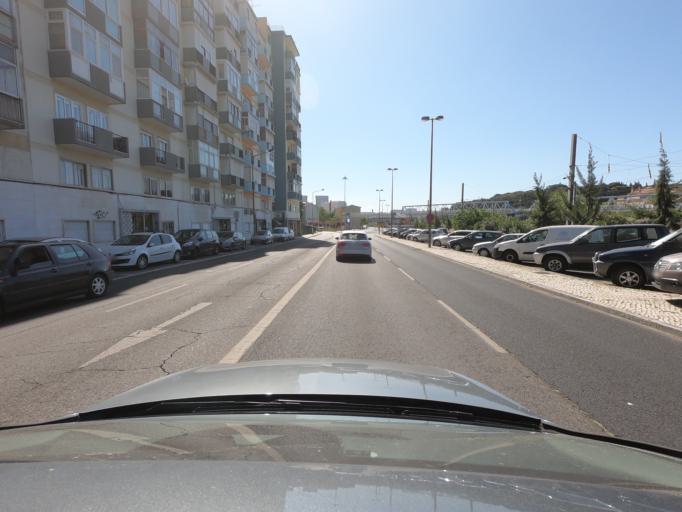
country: PT
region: Lisbon
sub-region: Odivelas
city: Pontinha
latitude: 38.7423
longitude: -9.1783
